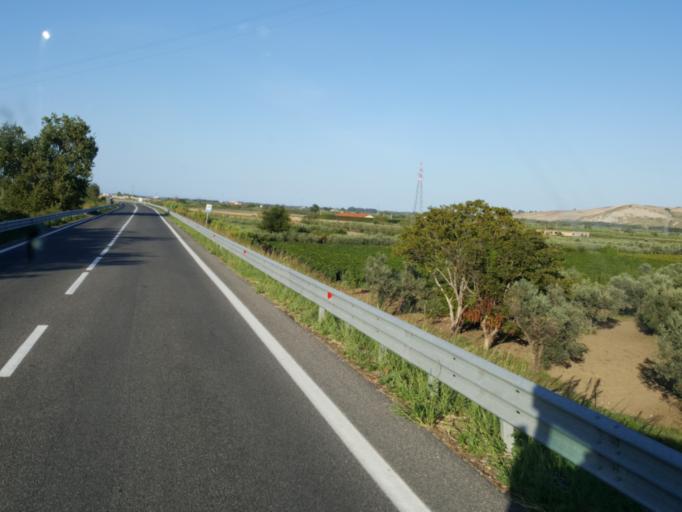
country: IT
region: Abruzzo
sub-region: Provincia di Chieti
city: San Salvo
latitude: 42.0392
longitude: 14.7543
